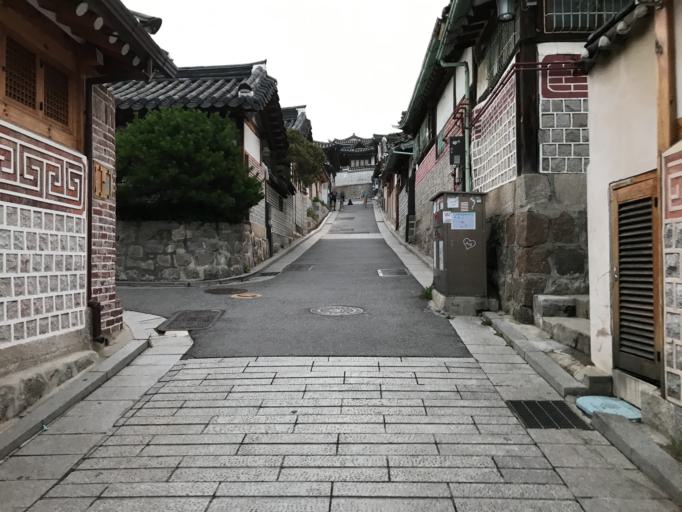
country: KR
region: Seoul
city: Seoul
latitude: 37.5829
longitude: 126.9836
